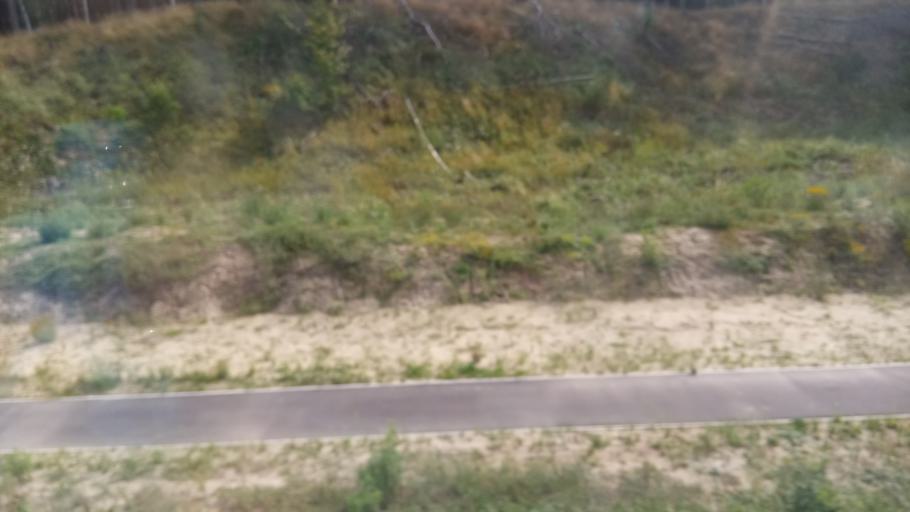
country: PL
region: Greater Poland Voivodeship
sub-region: Powiat pilski
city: Kaczory
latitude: 53.1113
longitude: 16.8504
